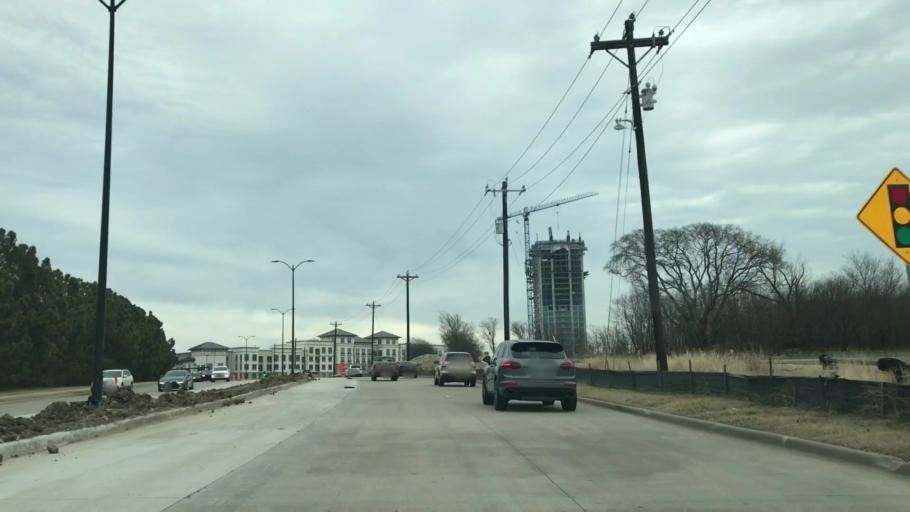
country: US
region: Texas
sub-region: Collin County
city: Frisco
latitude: 33.1164
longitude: -96.8331
